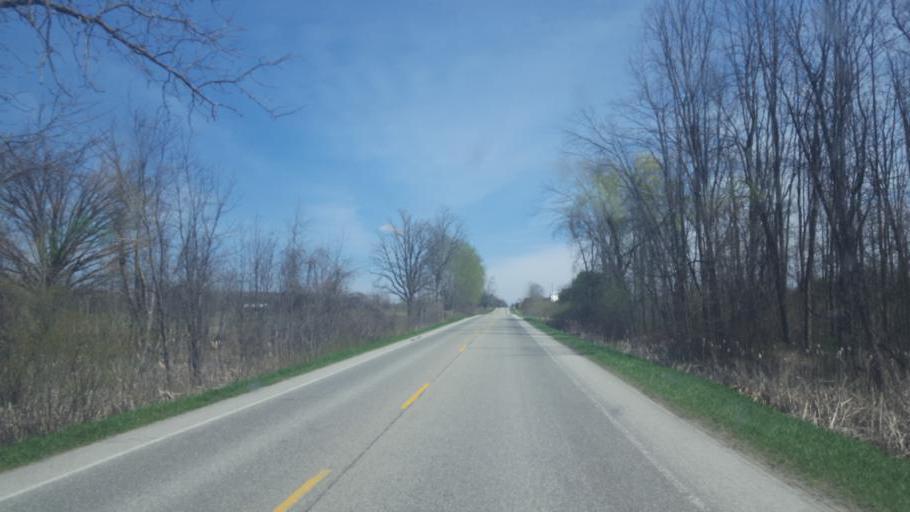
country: US
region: Michigan
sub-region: Midland County
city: Coleman
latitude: 43.8731
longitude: -84.6351
